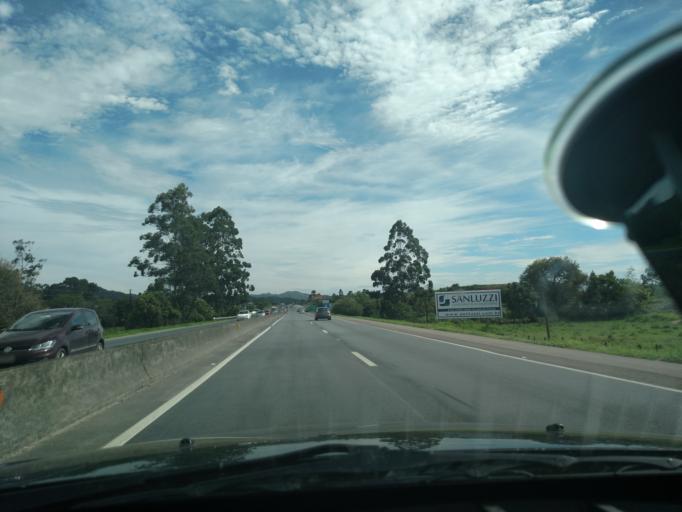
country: BR
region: Santa Catarina
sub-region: Biguacu
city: Biguacu
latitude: -27.4074
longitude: -48.6283
